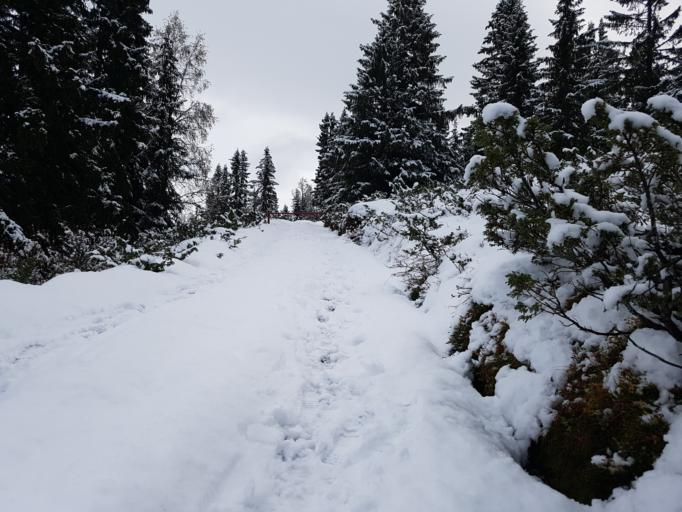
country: NO
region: Oppland
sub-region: Sel
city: Otta
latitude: 61.8071
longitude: 9.6762
